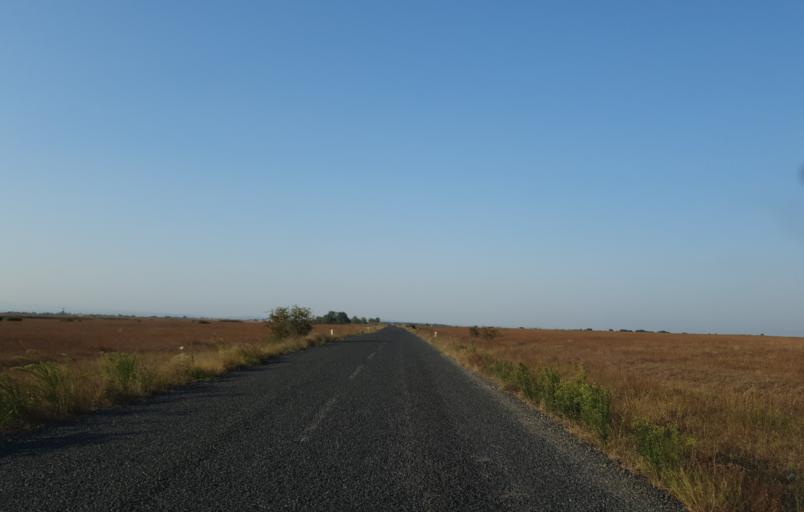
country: TR
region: Tekirdag
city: Beyazkoy
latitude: 41.4084
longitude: 27.7609
